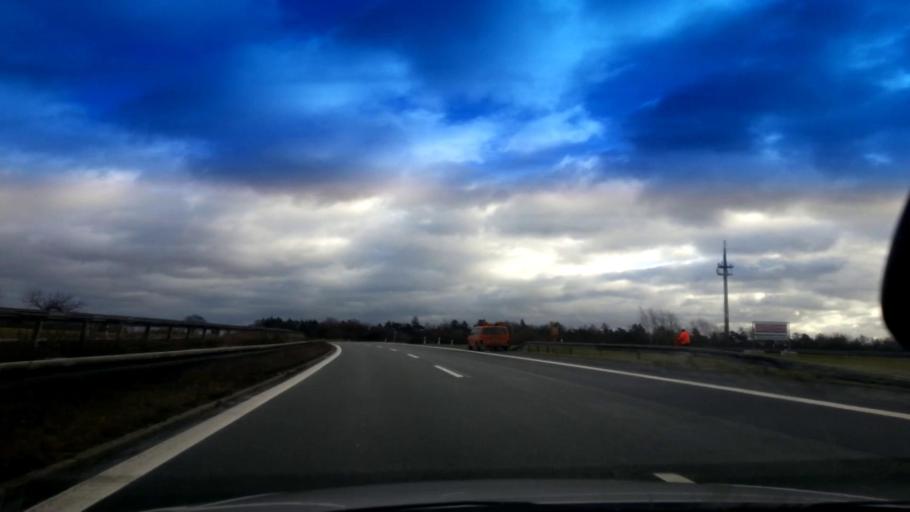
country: DE
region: Bavaria
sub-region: Upper Franconia
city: Eckersdorf
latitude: 50.0206
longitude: 11.4114
